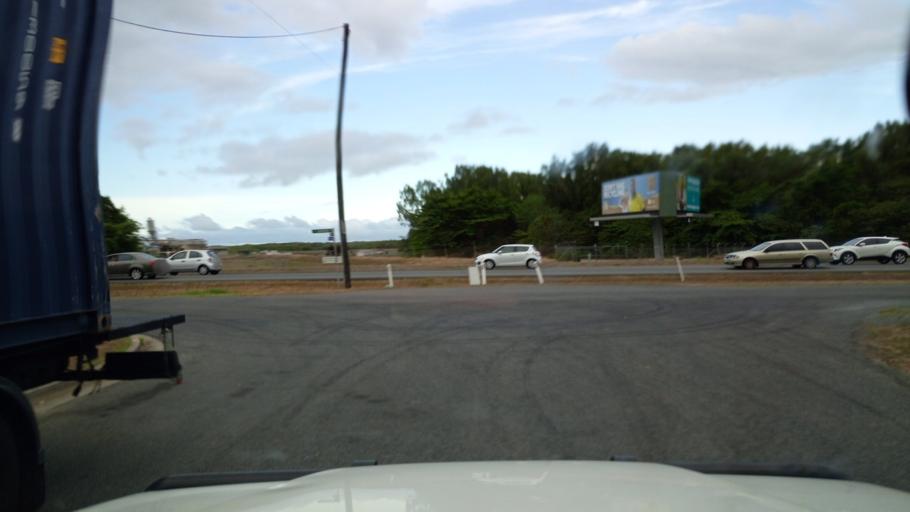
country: AU
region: Queensland
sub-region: Cairns
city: Redlynch
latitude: -16.8749
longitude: 145.7418
